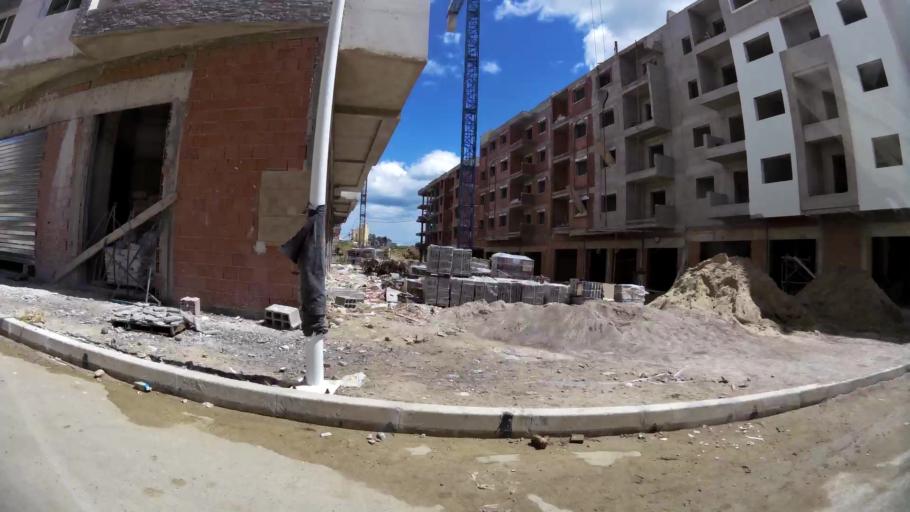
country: MA
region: Tanger-Tetouan
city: Tetouan
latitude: 35.5816
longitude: -5.3409
